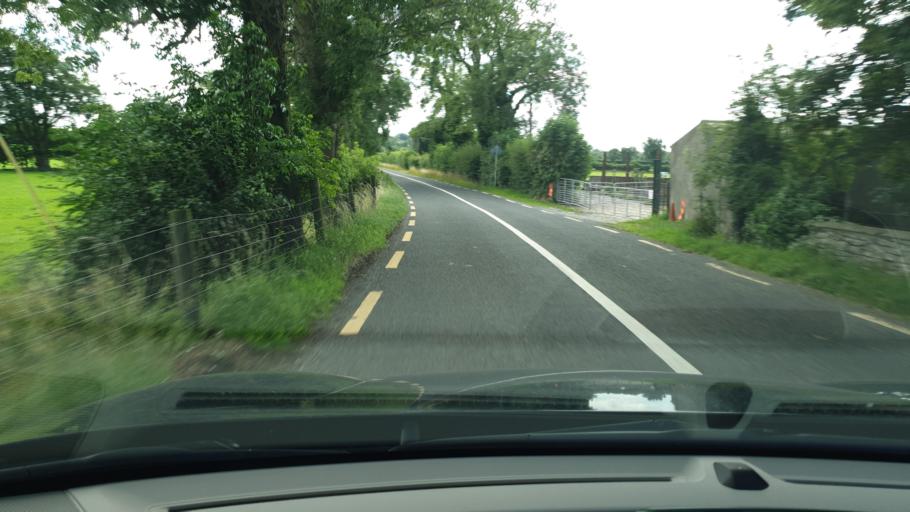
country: IE
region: Leinster
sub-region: Kildare
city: Kilcock
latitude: 53.4696
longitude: -6.6245
